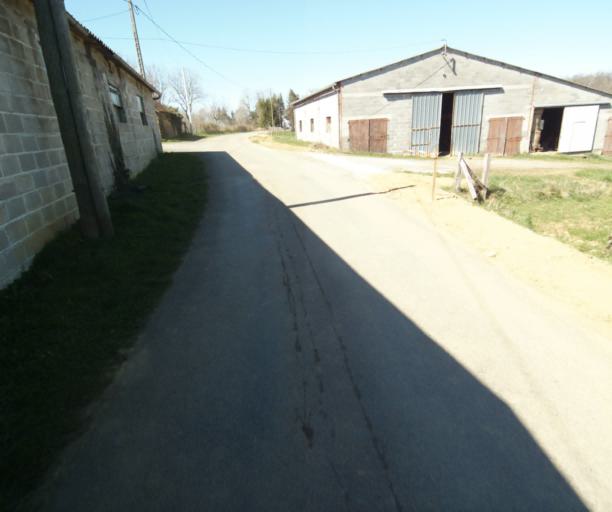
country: FR
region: Limousin
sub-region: Departement de la Correze
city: Saint-Clement
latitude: 45.3735
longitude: 1.6812
